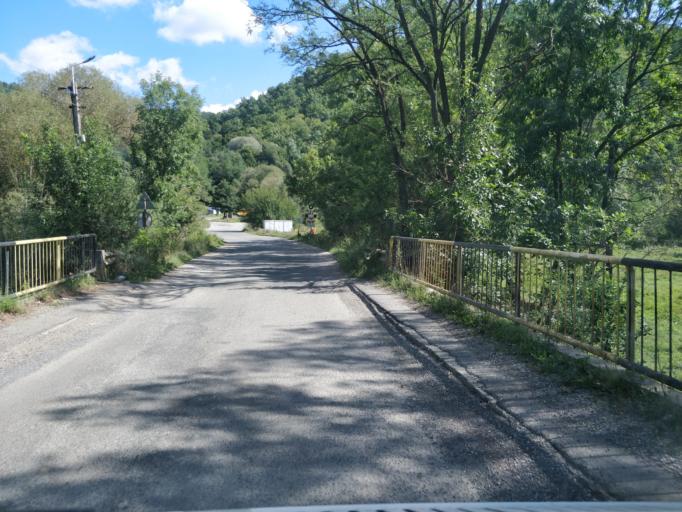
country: RO
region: Cluj
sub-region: Comuna Poeni
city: Poeni
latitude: 46.8927
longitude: 22.8796
